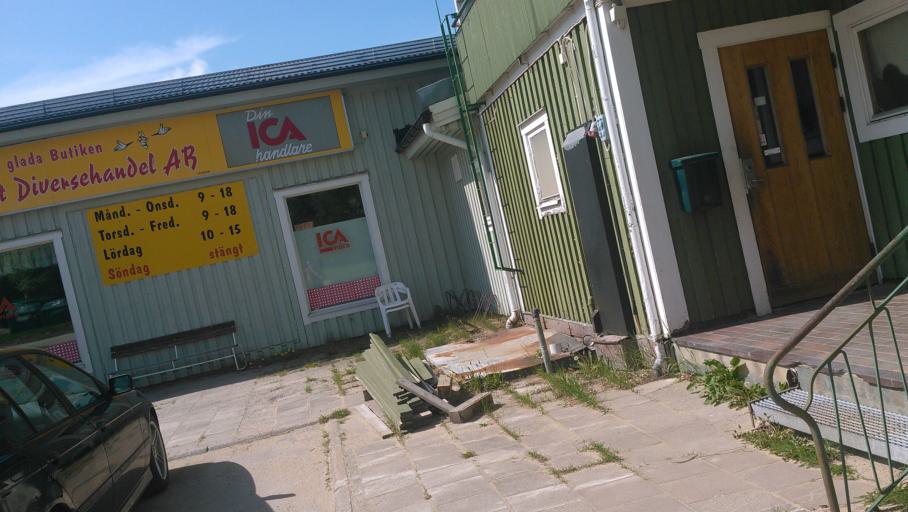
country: SE
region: Vaesterbotten
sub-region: Vannas Kommun
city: Vannasby
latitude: 63.8513
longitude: 19.9266
